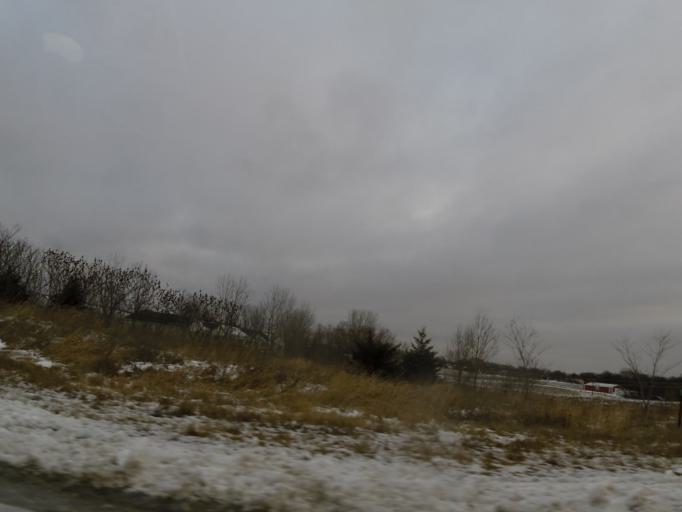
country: US
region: Minnesota
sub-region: Carver County
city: Chaska
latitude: 44.8071
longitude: -93.6235
